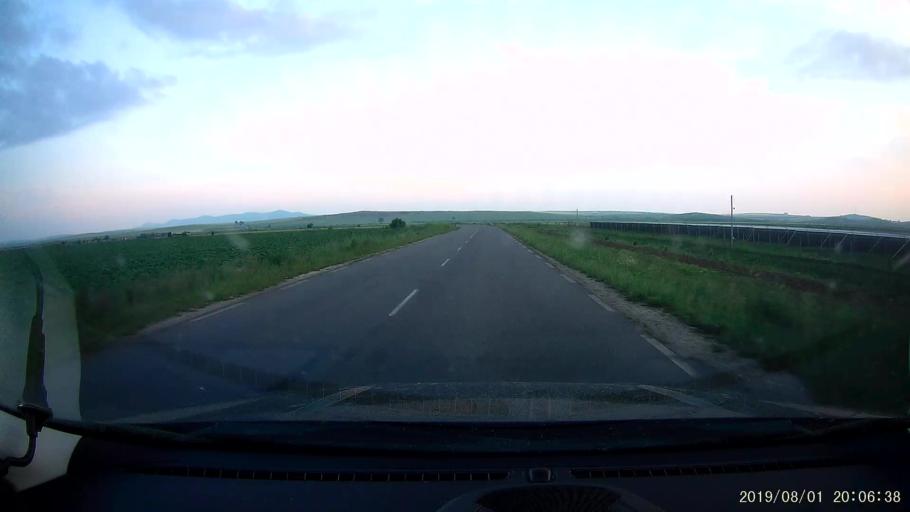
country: BG
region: Yambol
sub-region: Obshtina Yambol
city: Yambol
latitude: 42.5324
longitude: 26.5571
